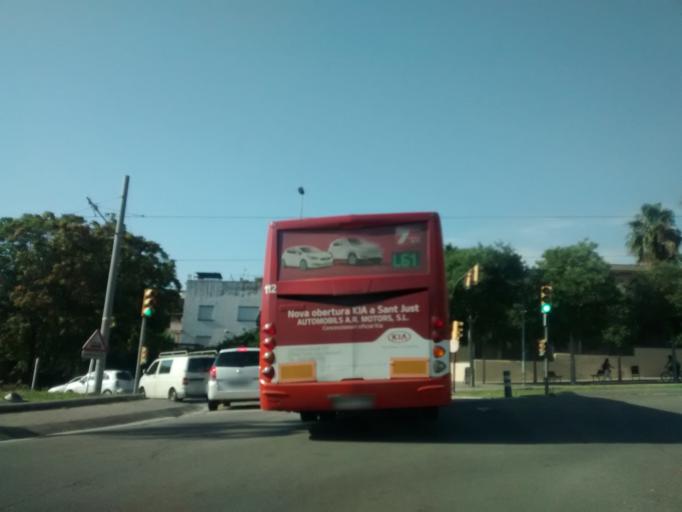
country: ES
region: Catalonia
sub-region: Provincia de Barcelona
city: Sant Just Desvern
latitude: 41.3789
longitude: 2.0720
